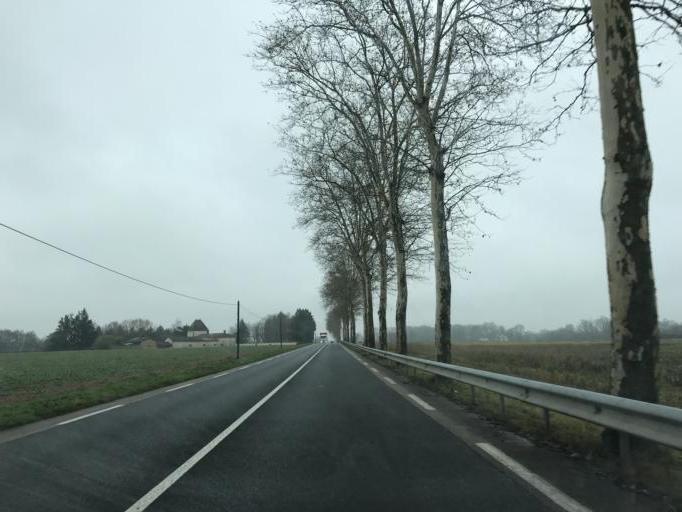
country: FR
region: Rhone-Alpes
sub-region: Departement de l'Ain
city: Saint-Paul-de-Varax
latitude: 46.0701
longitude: 5.0898
